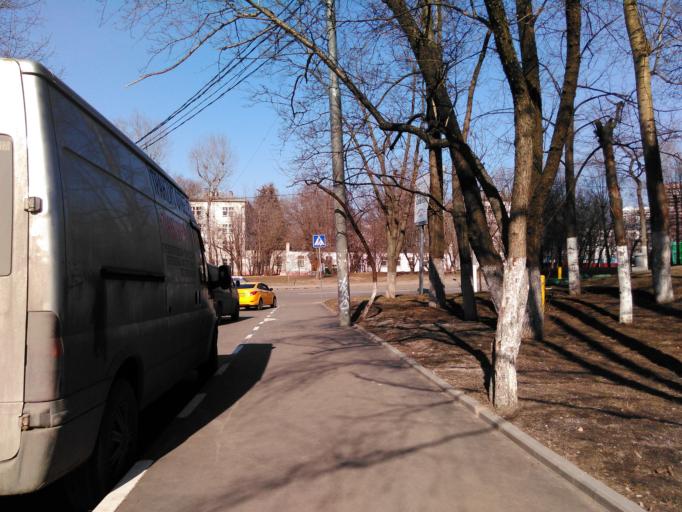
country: RU
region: Moskovskaya
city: Semenovskoye
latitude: 55.6698
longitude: 37.5217
